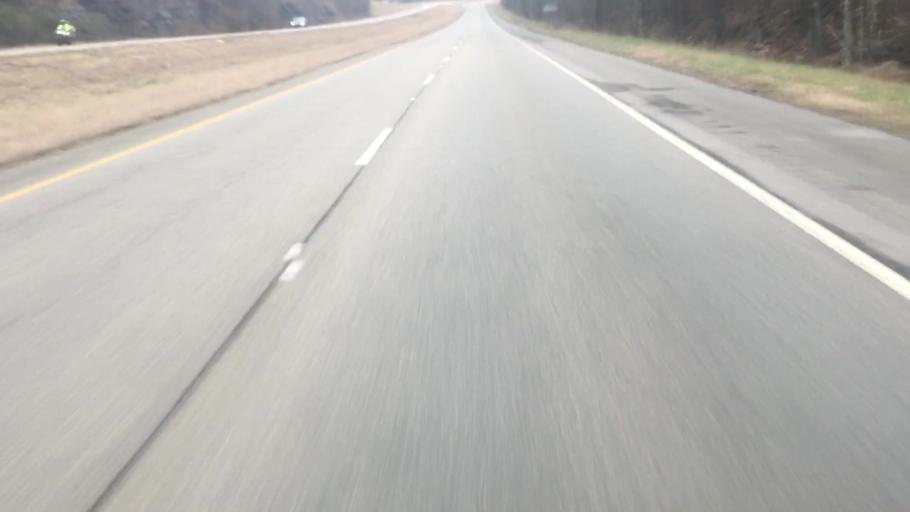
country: US
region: Alabama
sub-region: Walker County
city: Sumiton
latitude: 33.7771
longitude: -87.0804
